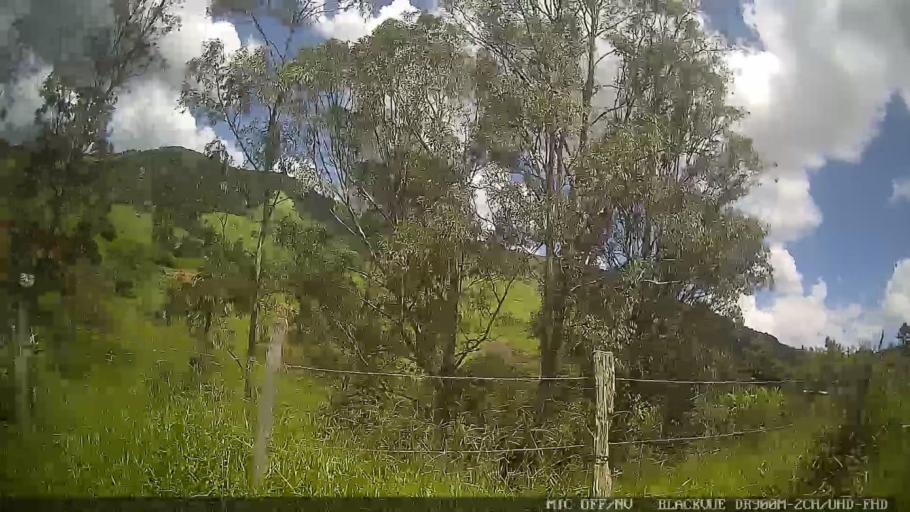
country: BR
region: Minas Gerais
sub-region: Extrema
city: Extrema
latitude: -22.8691
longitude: -46.2896
